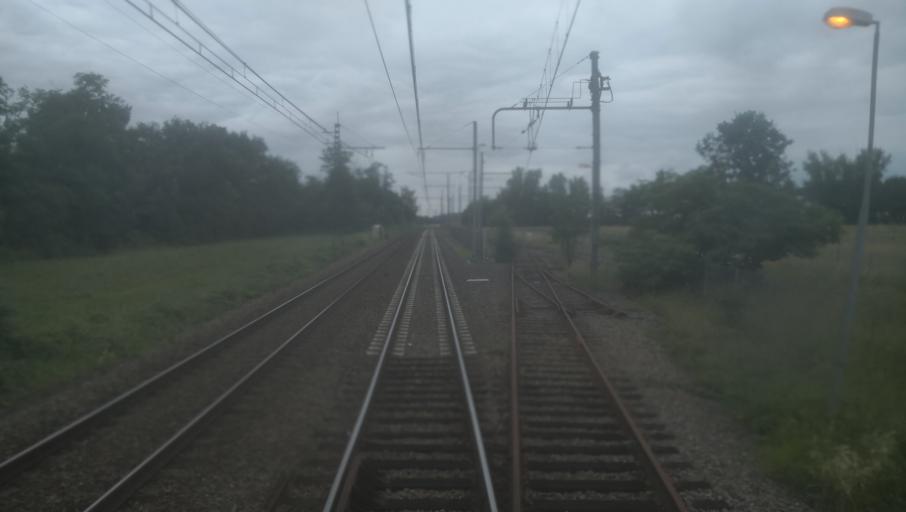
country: FR
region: Midi-Pyrenees
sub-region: Departement du Tarn-et-Garonne
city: Grisolles
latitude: 43.8421
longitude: 1.2923
